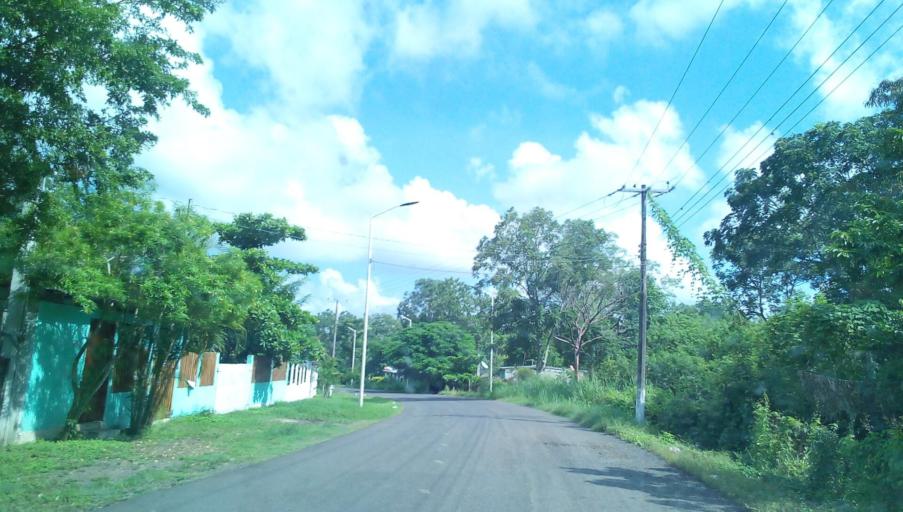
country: MX
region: Veracruz
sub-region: Citlaltepetl
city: Las Sabinas
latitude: 21.3573
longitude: -97.8995
